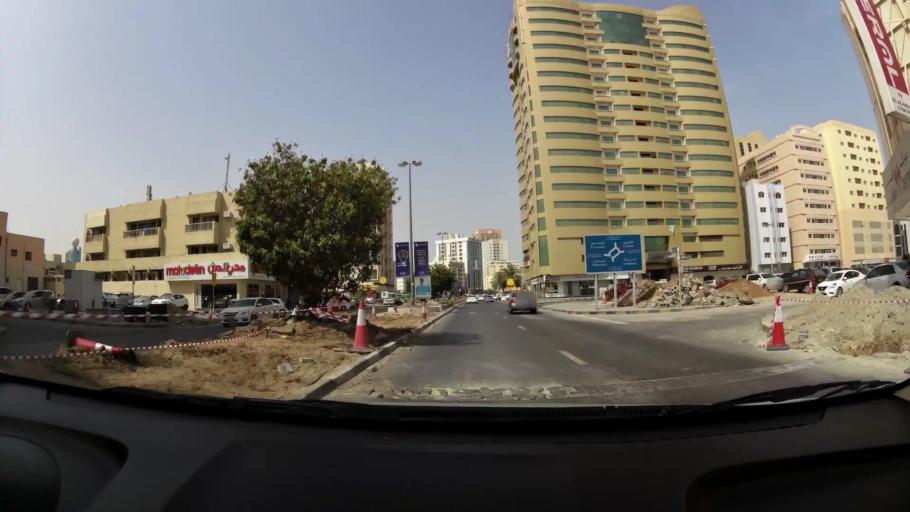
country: AE
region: Ash Shariqah
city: Sharjah
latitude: 25.3626
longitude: 55.3983
